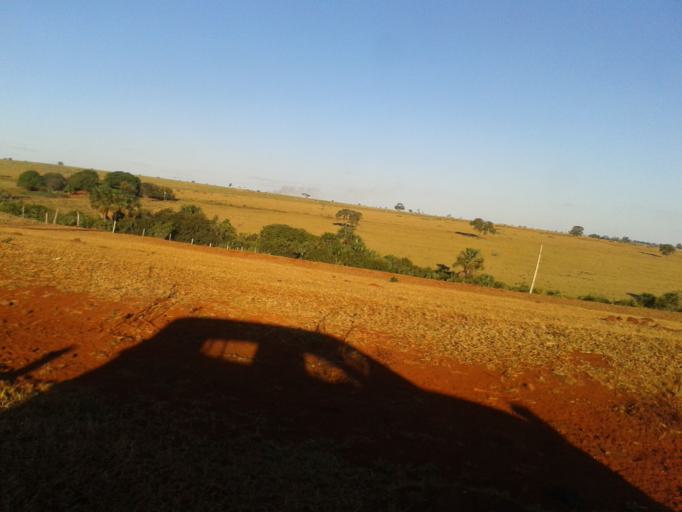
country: BR
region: Minas Gerais
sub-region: Centralina
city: Centralina
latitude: -18.7626
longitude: -49.2013
